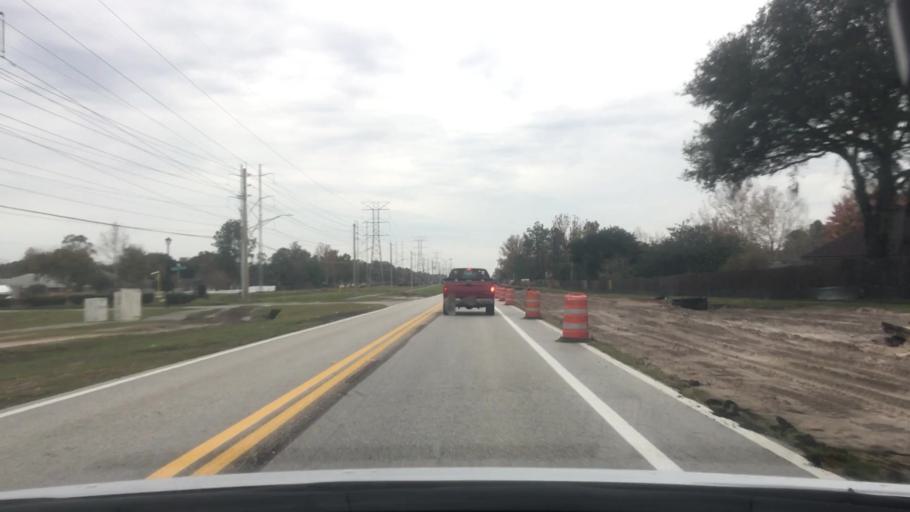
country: US
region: Florida
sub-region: Duval County
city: Atlantic Beach
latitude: 30.3515
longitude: -81.4900
